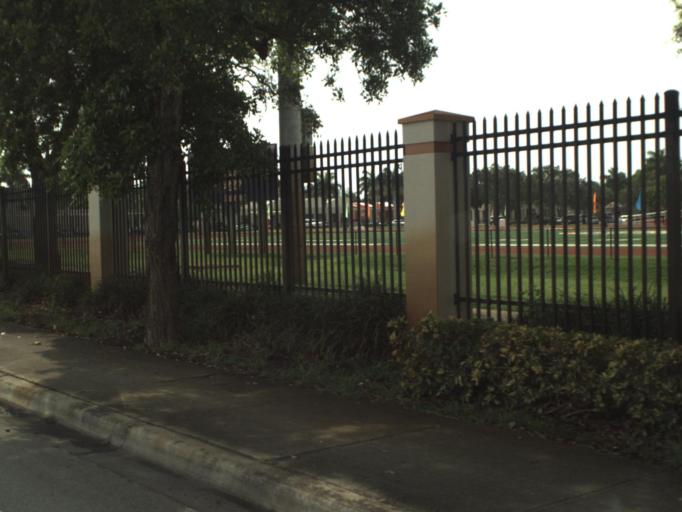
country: US
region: Florida
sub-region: Broward County
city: Roosevelt Gardens
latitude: 26.1365
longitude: -80.1634
